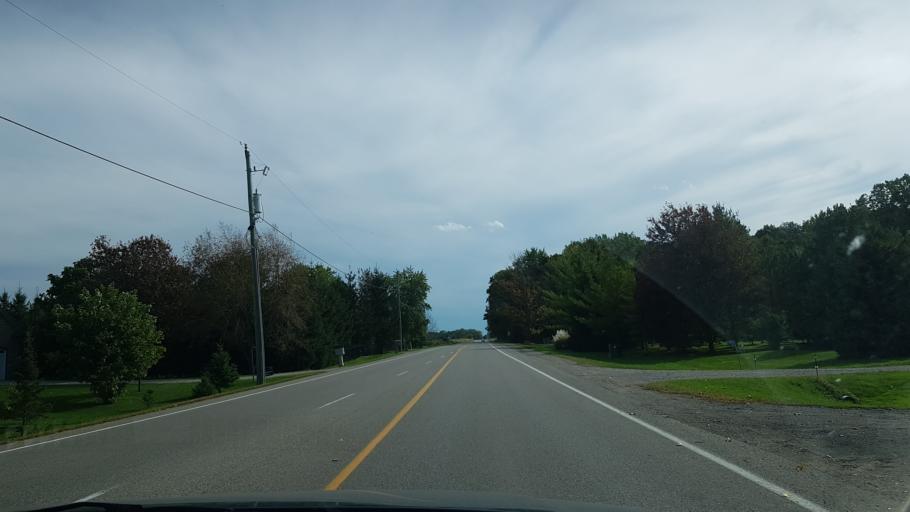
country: CA
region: Ontario
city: Delaware
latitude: 42.9987
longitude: -81.3952
